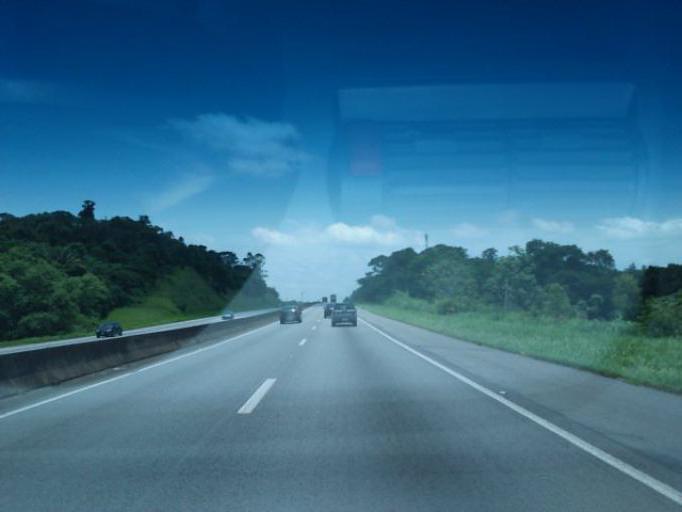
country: BR
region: Sao Paulo
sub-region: Registro
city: Registro
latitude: -24.4387
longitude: -47.7956
